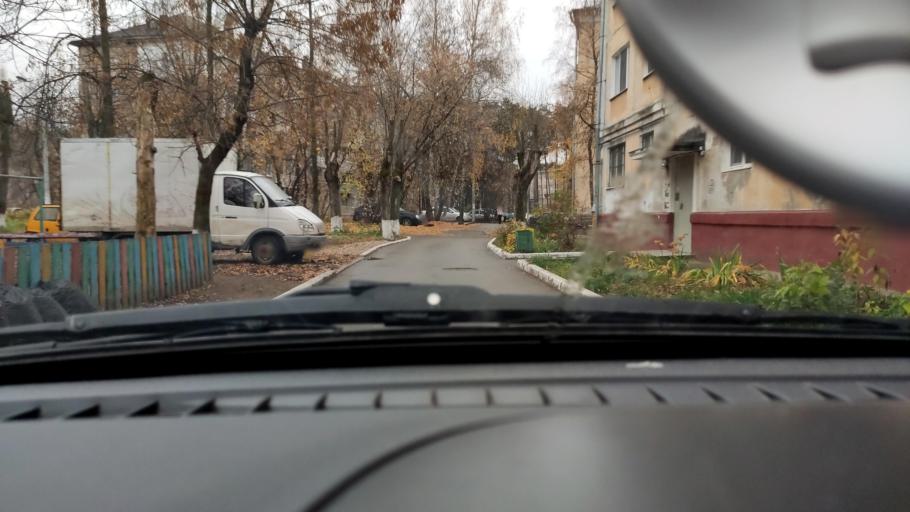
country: RU
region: Perm
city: Kultayevo
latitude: 58.0140
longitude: 55.9685
